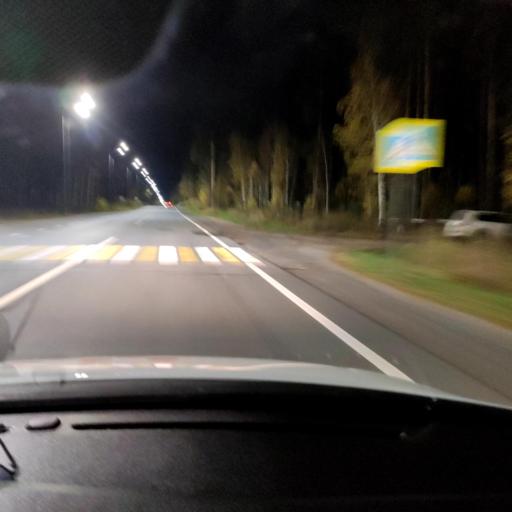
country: RU
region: Tatarstan
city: Stolbishchi
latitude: 55.6364
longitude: 49.0639
